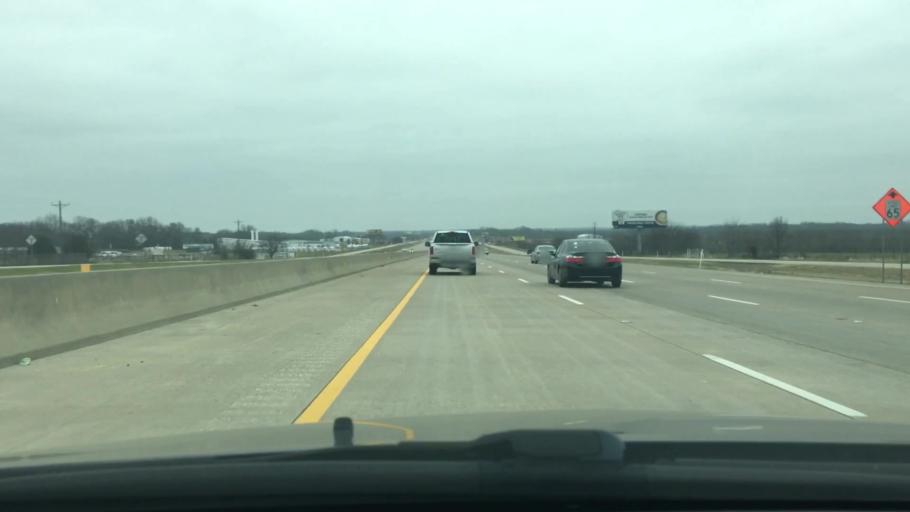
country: US
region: Texas
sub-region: Navarro County
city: Corsicana
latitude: 32.1954
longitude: -96.4734
